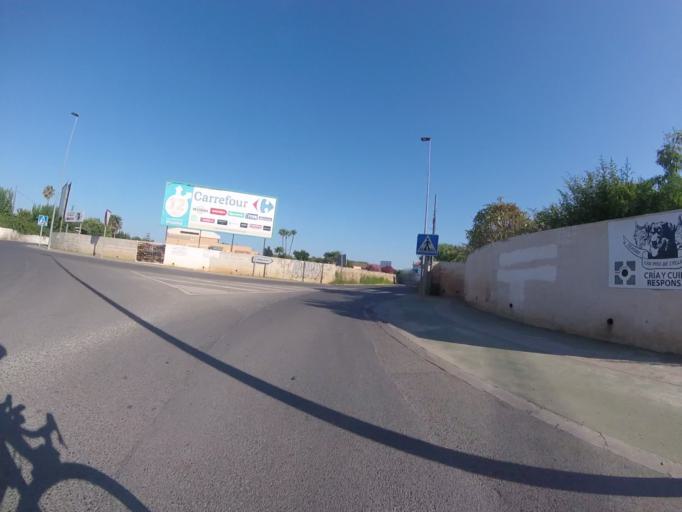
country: ES
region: Valencia
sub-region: Provincia de Castello
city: Benicarlo
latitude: 40.4009
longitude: 0.4148
